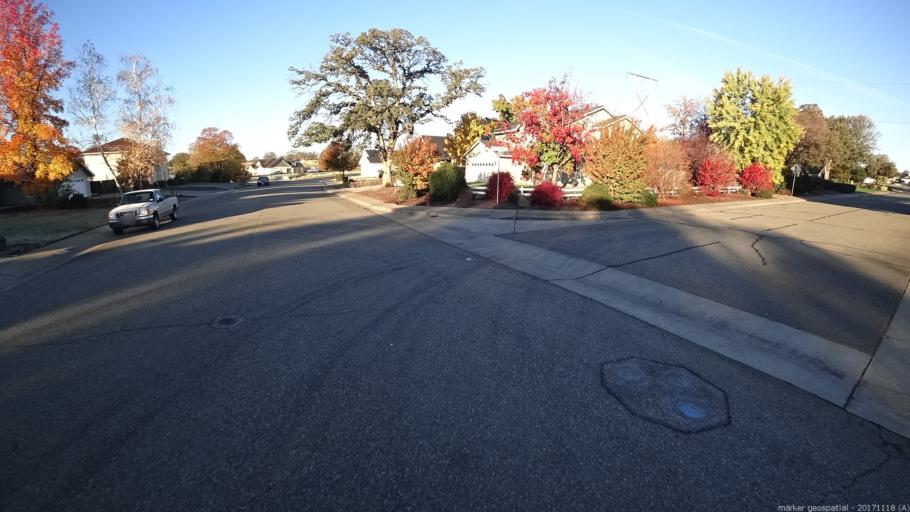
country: US
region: California
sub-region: Shasta County
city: Cottonwood
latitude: 40.3969
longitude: -122.2932
